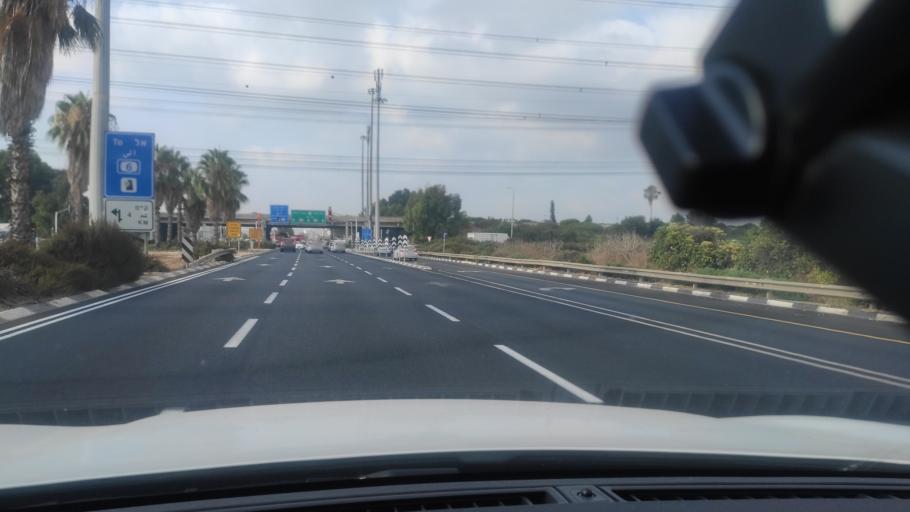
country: IL
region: Central District
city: Hod HaSharon
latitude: 32.1233
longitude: 34.9036
